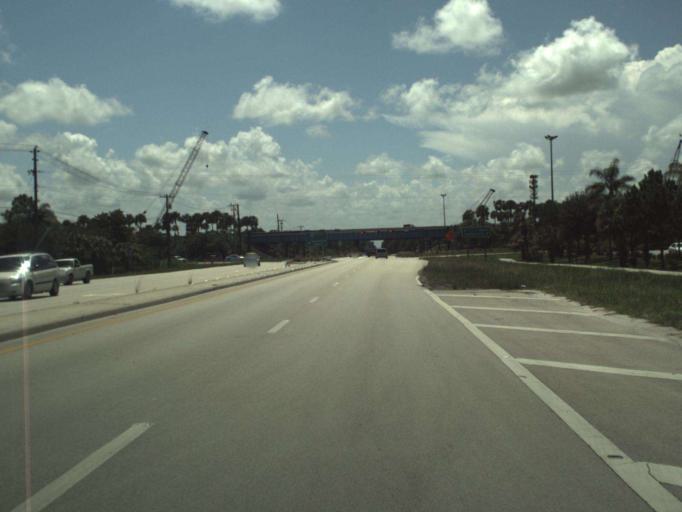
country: US
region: Florida
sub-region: Indian River County
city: Fellsmere
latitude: 27.7676
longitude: -80.5481
